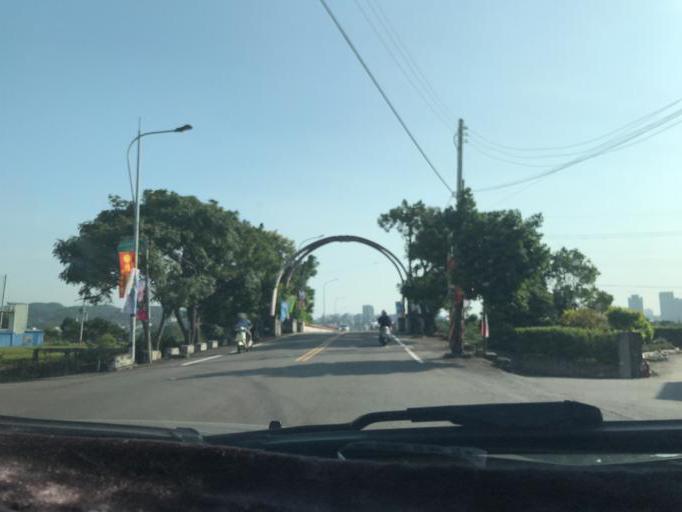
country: TW
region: Taiwan
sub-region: Hsinchu
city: Zhubei
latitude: 24.8394
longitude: 121.0364
